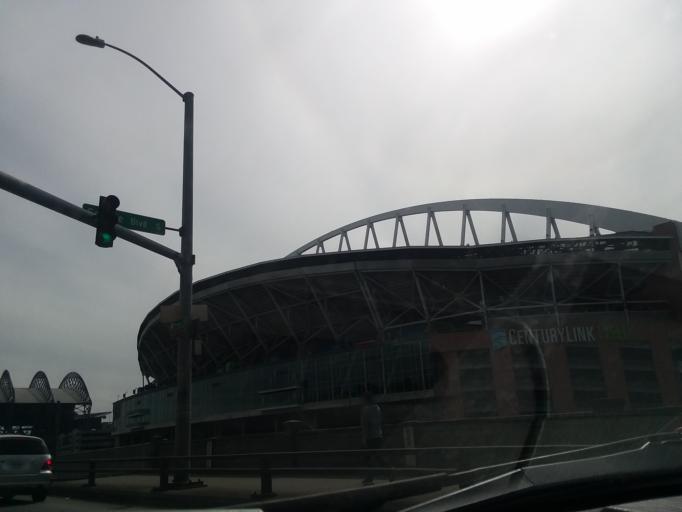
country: US
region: Washington
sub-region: King County
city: Seattle
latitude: 47.5965
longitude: -122.3292
